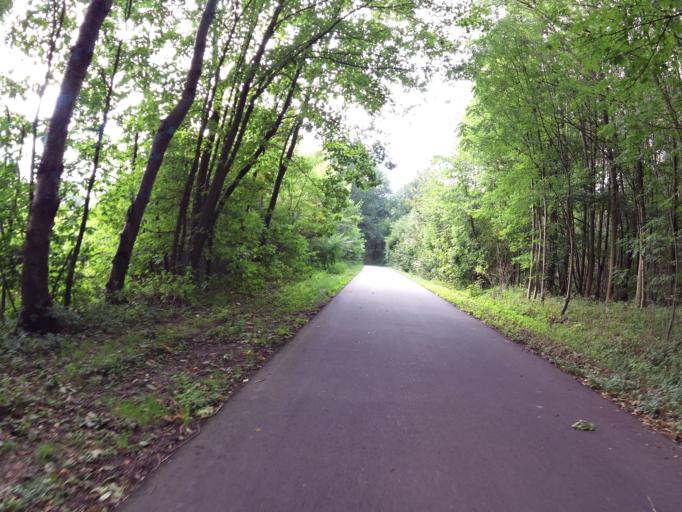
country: BE
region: Flanders
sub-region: Provincie Limburg
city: Lanaken
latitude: 50.8870
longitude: 5.6572
